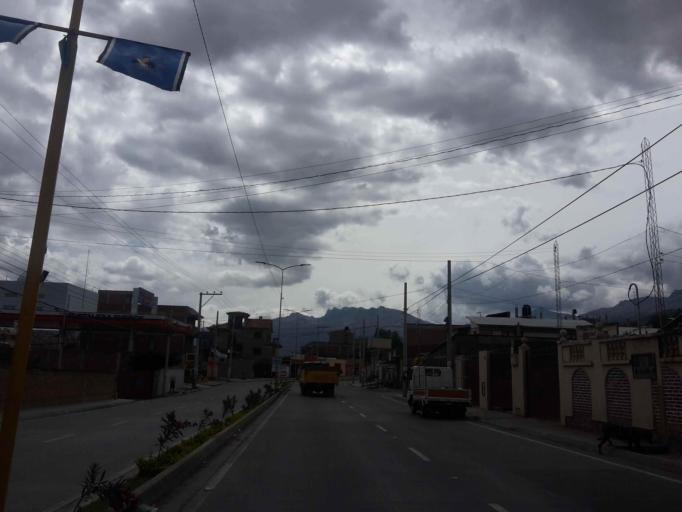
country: BO
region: Cochabamba
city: Cochabamba
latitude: -17.3487
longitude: -66.1900
